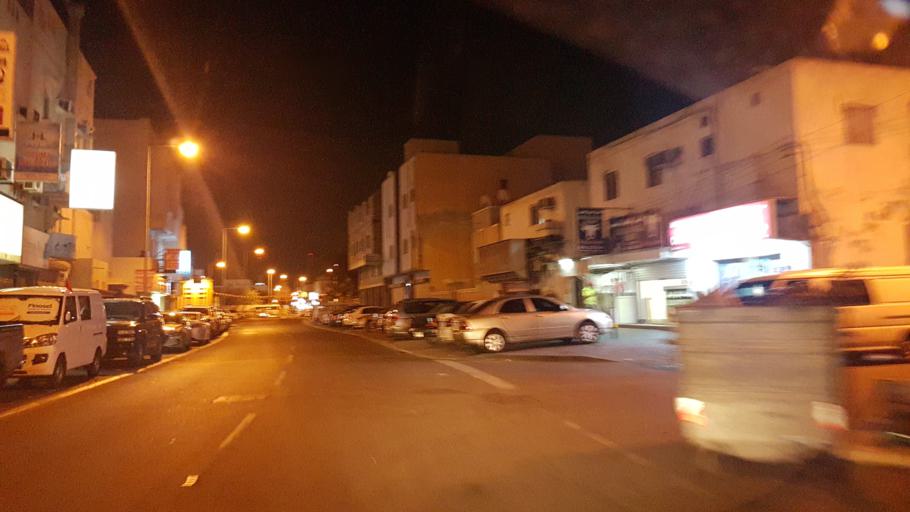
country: BH
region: Muharraq
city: Al Hadd
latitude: 26.2432
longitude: 50.6556
